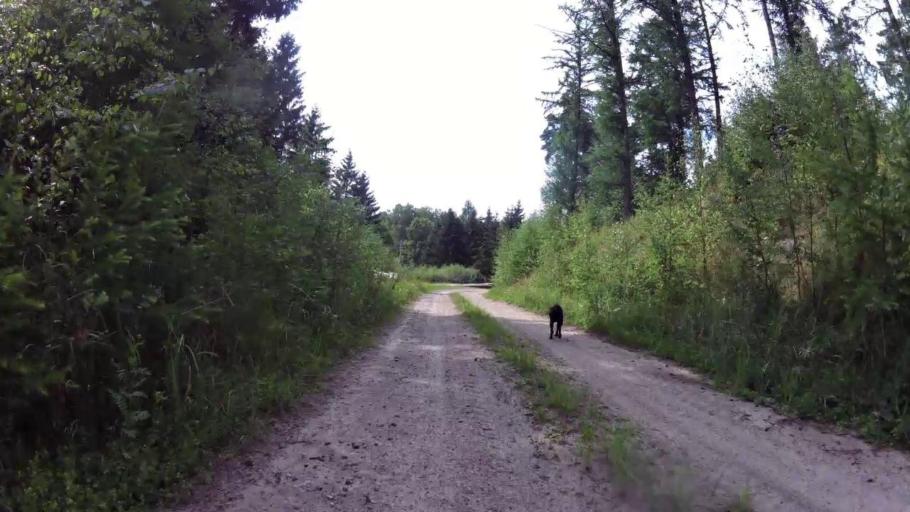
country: PL
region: West Pomeranian Voivodeship
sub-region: Powiat lobeski
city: Wegorzyno
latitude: 53.5247
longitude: 15.6441
